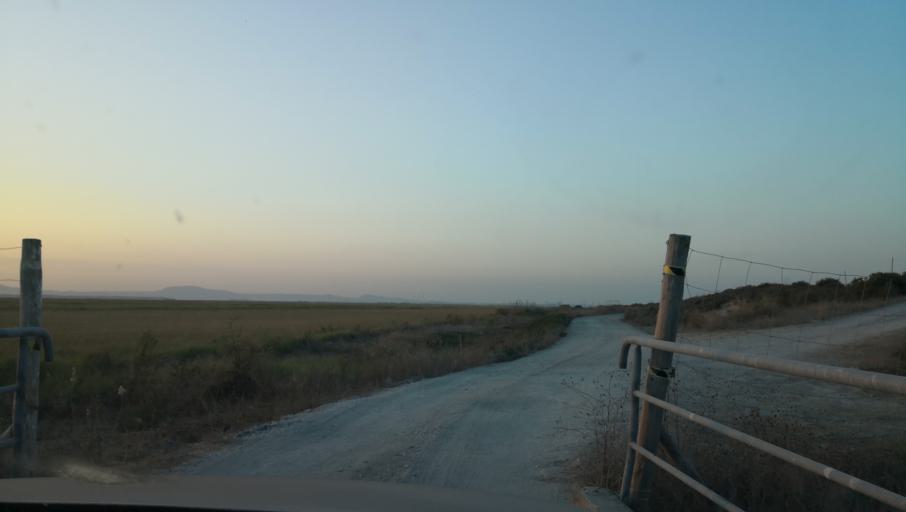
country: PT
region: Setubal
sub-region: Setubal
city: Setubal
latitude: 38.4005
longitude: -8.7735
